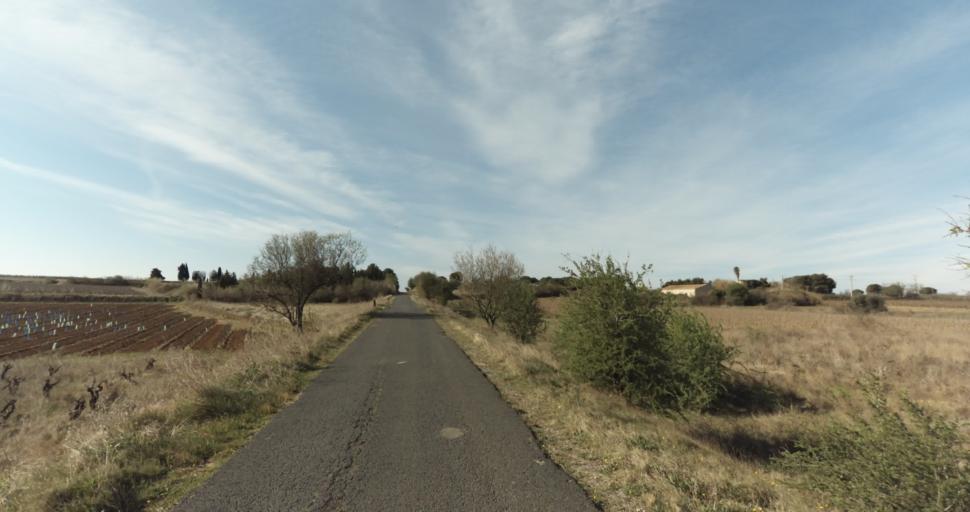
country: FR
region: Languedoc-Roussillon
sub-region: Departement de l'Herault
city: Marseillan
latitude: 43.3503
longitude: 3.5172
